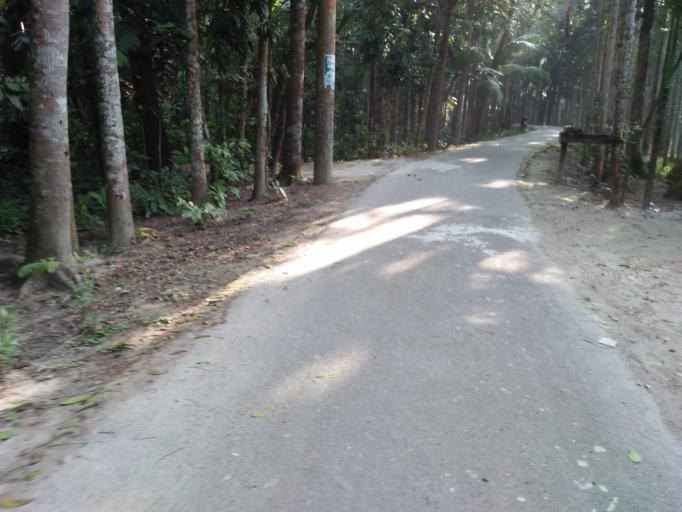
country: BD
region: Barisal
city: Bhola
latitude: 22.6763
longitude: 90.6389
